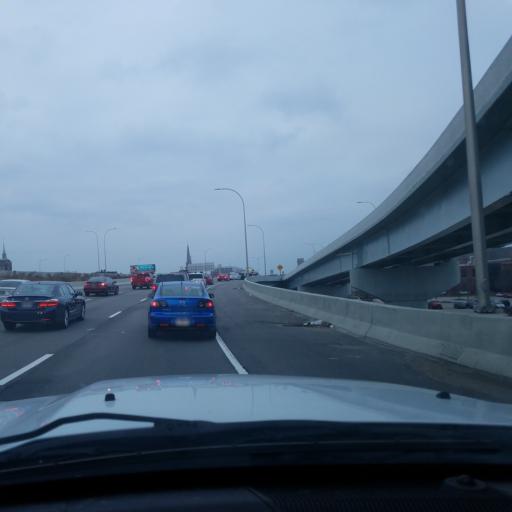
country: US
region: Kentucky
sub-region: Jefferson County
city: Louisville
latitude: 38.2572
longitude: -85.7423
